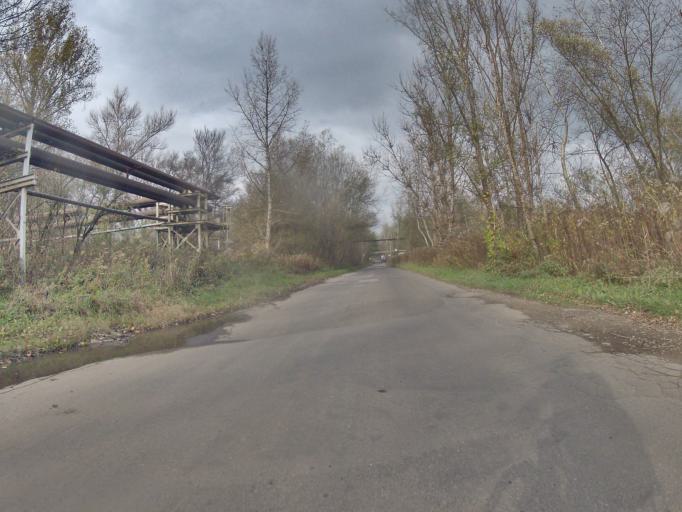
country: PL
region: Lesser Poland Voivodeship
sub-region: Powiat wielicki
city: Wegrzce Wielkie
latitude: 50.0631
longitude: 20.1025
